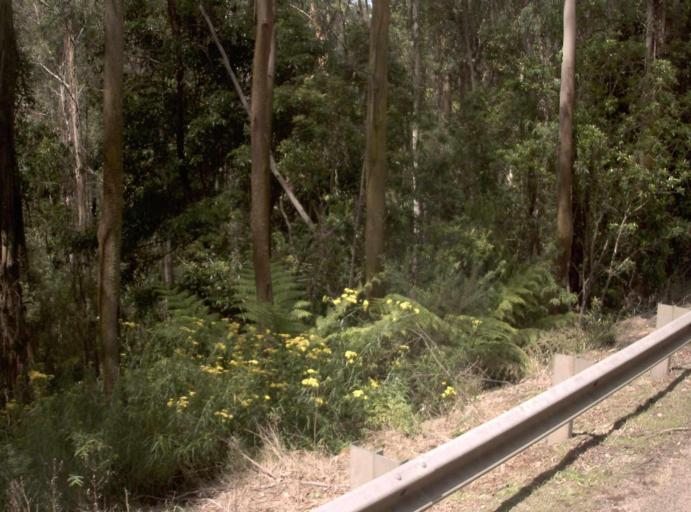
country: AU
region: New South Wales
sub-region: Bombala
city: Bombala
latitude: -37.5360
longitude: 149.3815
